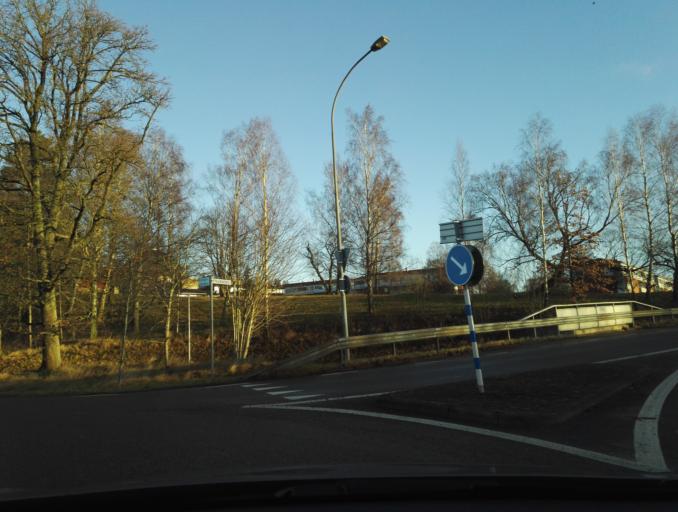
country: SE
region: Kronoberg
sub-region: Vaxjo Kommun
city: Vaexjoe
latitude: 56.8988
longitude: 14.7991
